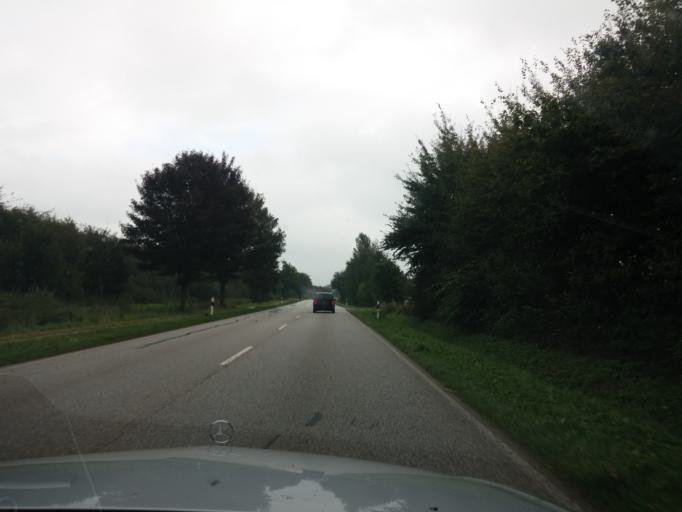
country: DE
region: Schleswig-Holstein
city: Treia
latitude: 54.5156
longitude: 9.3372
